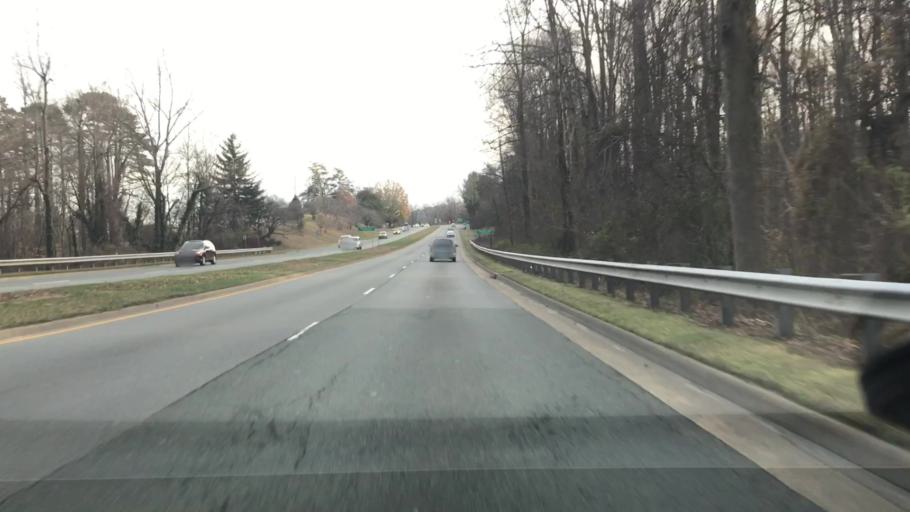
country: US
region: Virginia
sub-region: City of Charlottesville
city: Charlottesville
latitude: 38.0502
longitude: -78.4807
